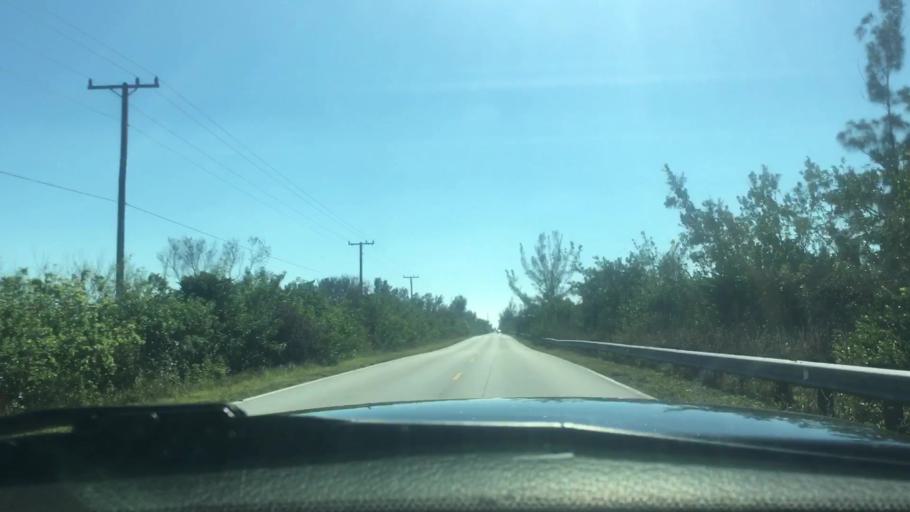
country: US
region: Florida
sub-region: Miami-Dade County
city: Florida City
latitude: 25.3700
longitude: -80.4319
